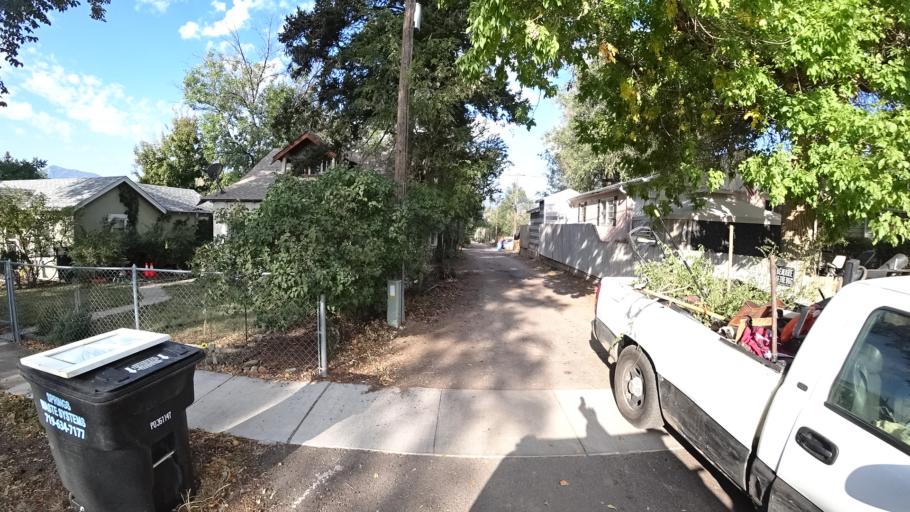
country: US
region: Colorado
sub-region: El Paso County
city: Colorado Springs
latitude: 38.8270
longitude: -104.8060
